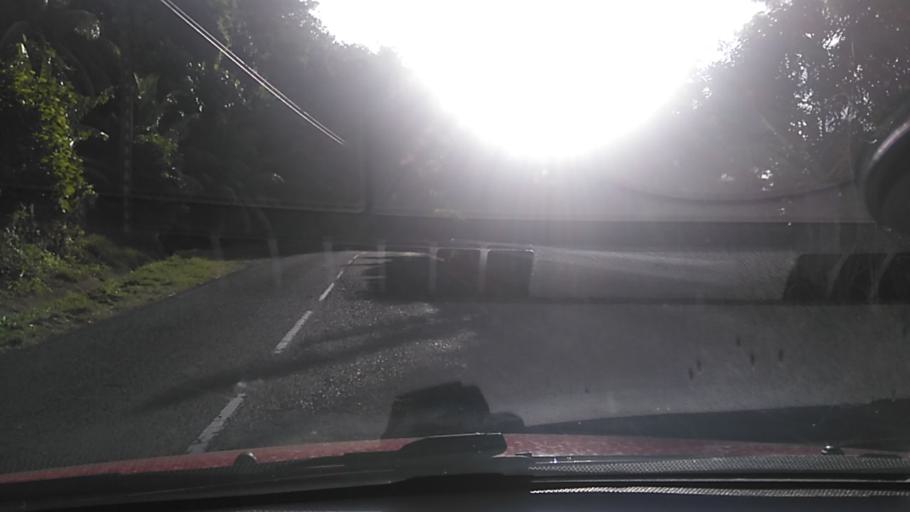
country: MQ
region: Martinique
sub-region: Martinique
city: Saint-Esprit
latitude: 14.5678
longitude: -60.9496
